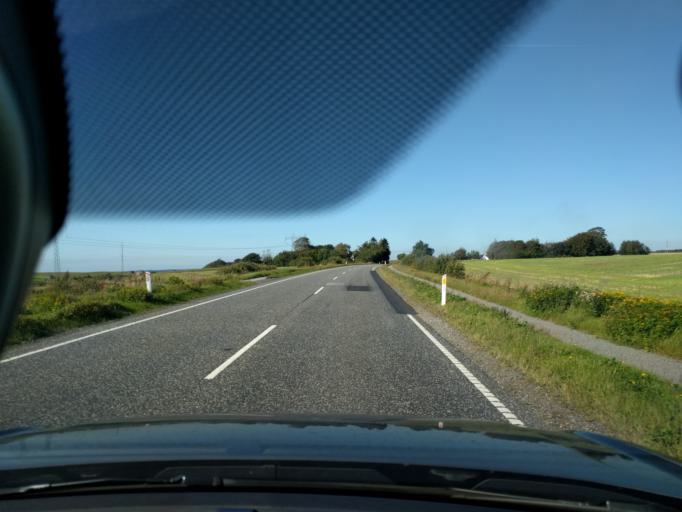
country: DK
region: North Denmark
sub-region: Vesthimmerland Kommune
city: Alestrup
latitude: 56.7158
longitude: 9.6141
